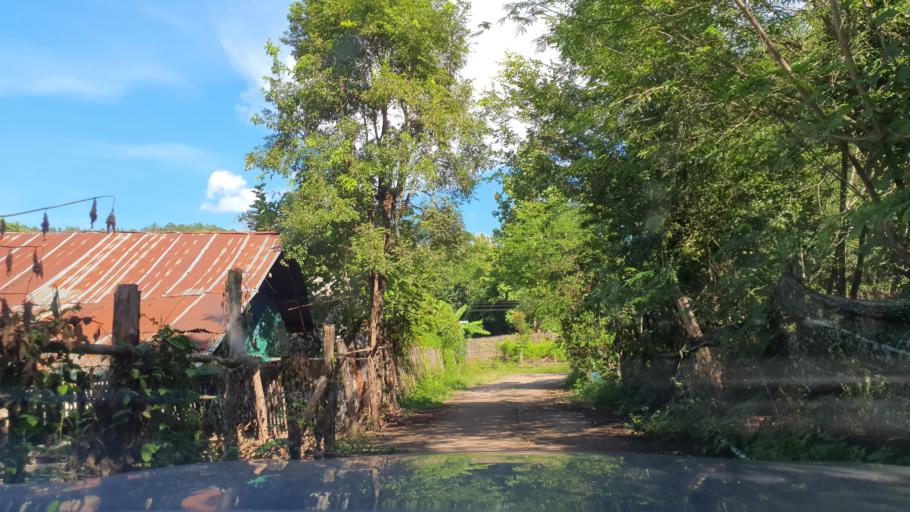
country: TH
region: Chiang Mai
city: Mae On
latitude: 18.7292
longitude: 99.3041
